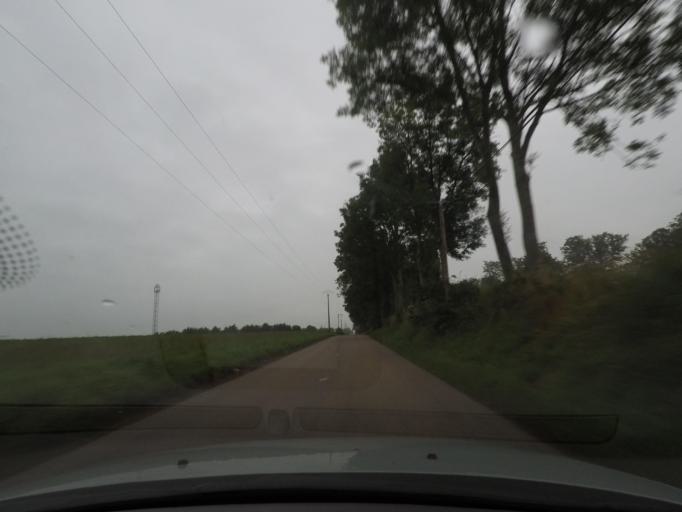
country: FR
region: Haute-Normandie
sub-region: Departement de la Seine-Maritime
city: Saint-Martin-Osmonville
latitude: 49.6038
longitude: 1.2441
